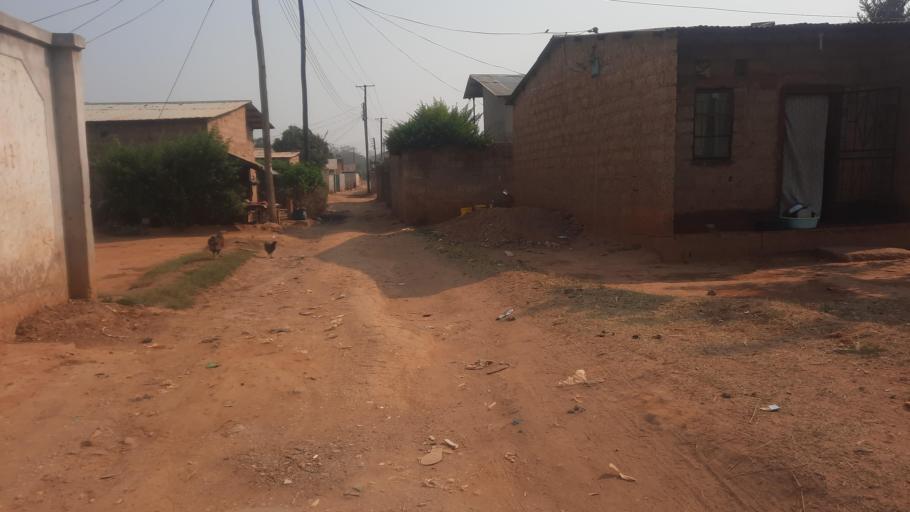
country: ZM
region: Lusaka
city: Lusaka
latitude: -15.3938
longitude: 28.3838
